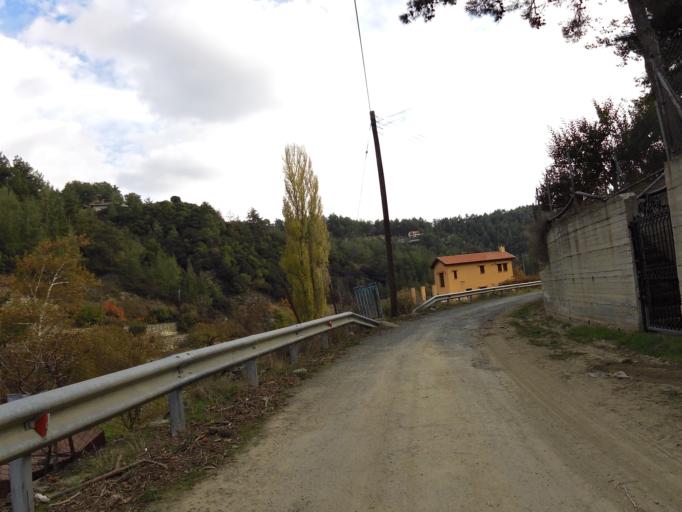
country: CY
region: Limassol
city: Kyperounta
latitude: 34.9323
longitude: 32.9353
